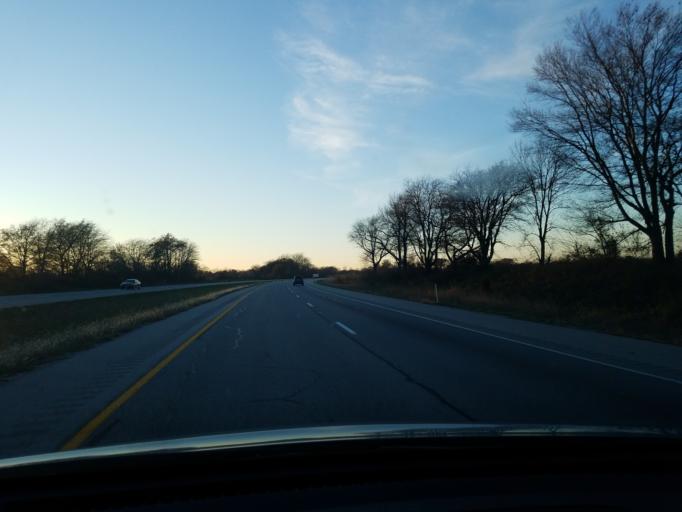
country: US
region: Indiana
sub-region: Posey County
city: Poseyville
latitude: 38.1846
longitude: -87.8158
